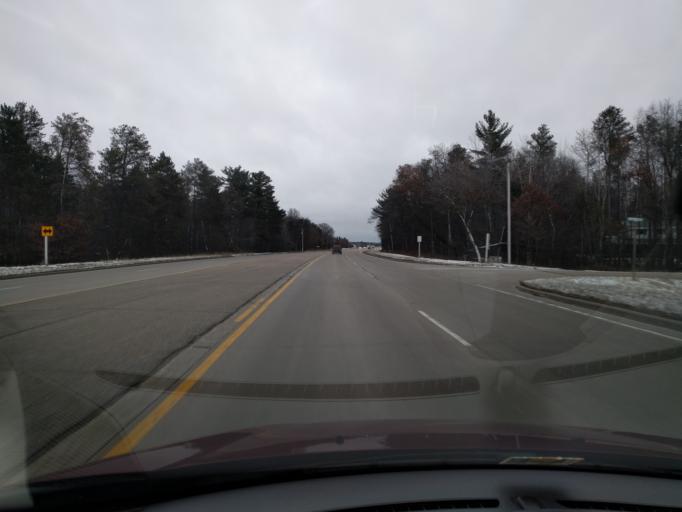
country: US
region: Wisconsin
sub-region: Portage County
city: Whiting
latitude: 44.5236
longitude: -89.4921
